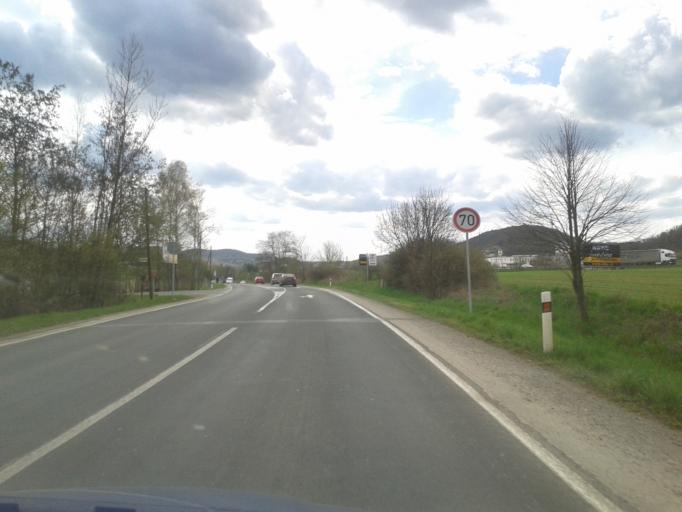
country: CZ
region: Central Bohemia
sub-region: Okres Beroun
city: Lodenice
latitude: 50.0039
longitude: 14.1740
